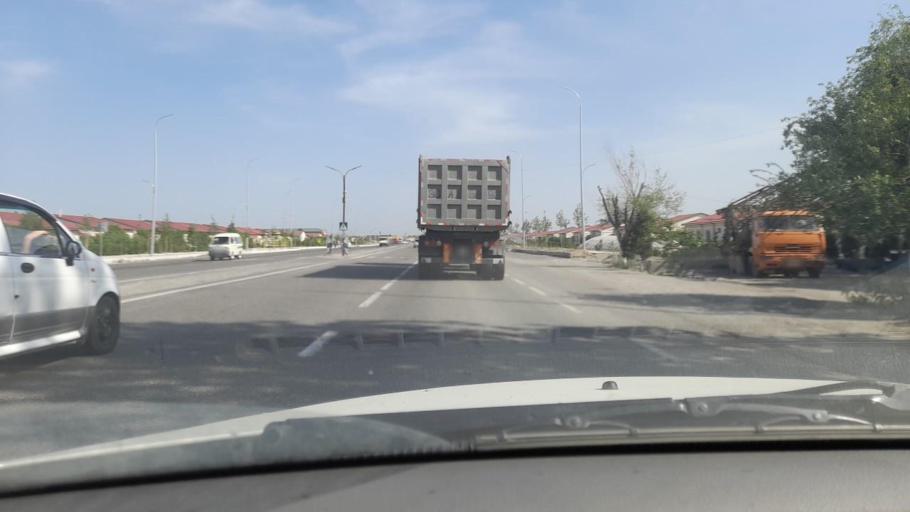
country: UZ
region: Samarqand
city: Daxbet
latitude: 39.7347
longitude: 66.9331
